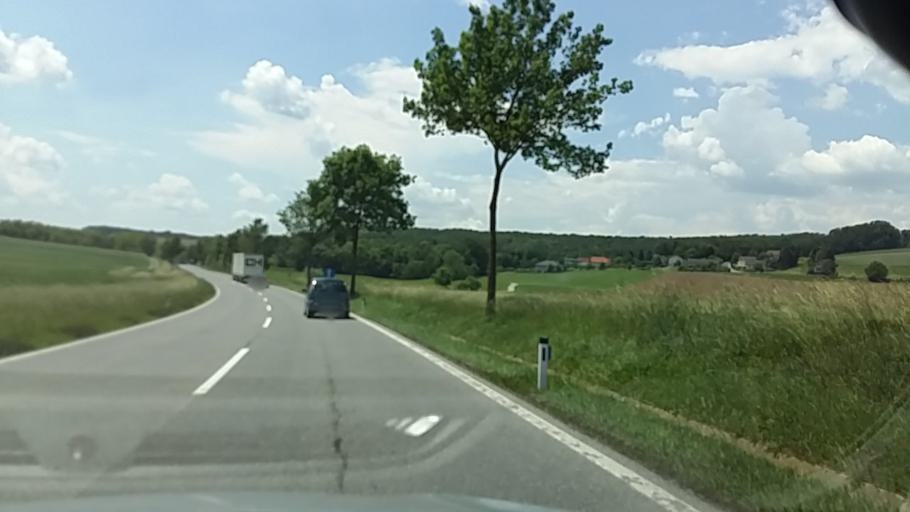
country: AT
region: Burgenland
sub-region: Politischer Bezirk Oberwart
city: Mariasdorf
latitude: 47.3523
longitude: 16.2295
